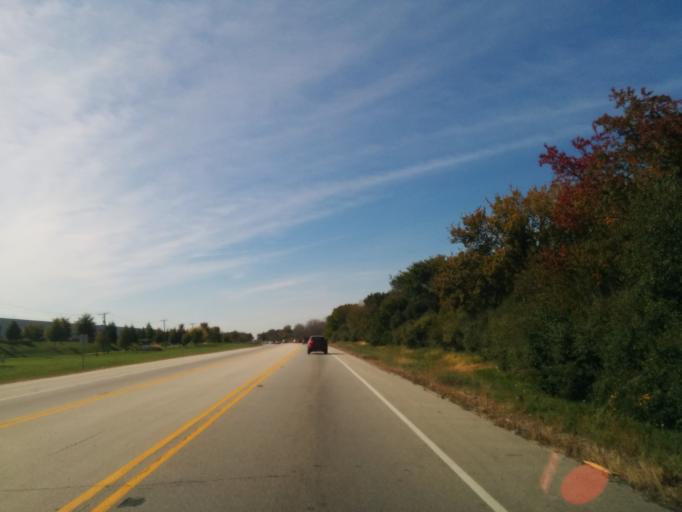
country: US
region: Illinois
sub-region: DuPage County
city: Warrenville
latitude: 41.8205
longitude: -88.2259
